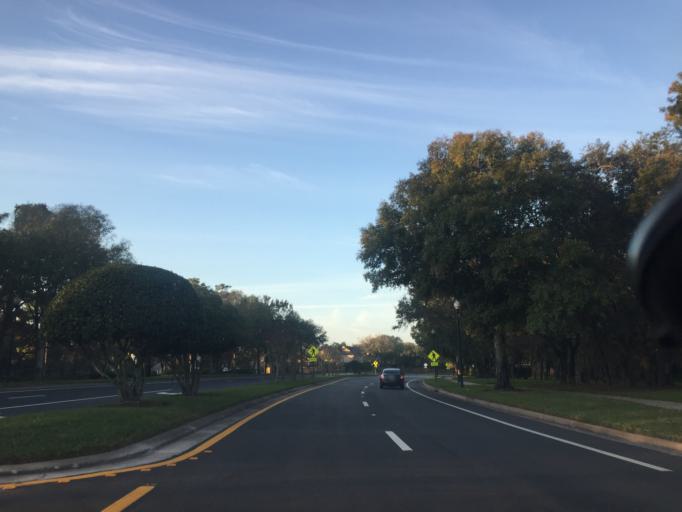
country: US
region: Florida
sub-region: Seminole County
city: Oviedo
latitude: 28.6179
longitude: -81.1858
